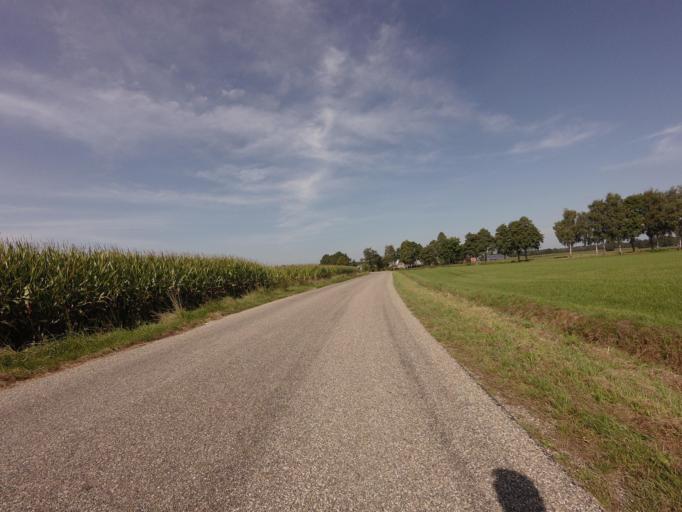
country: NL
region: Overijssel
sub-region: Gemeente Hof van Twente
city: Goor
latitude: 52.2535
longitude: 6.6293
